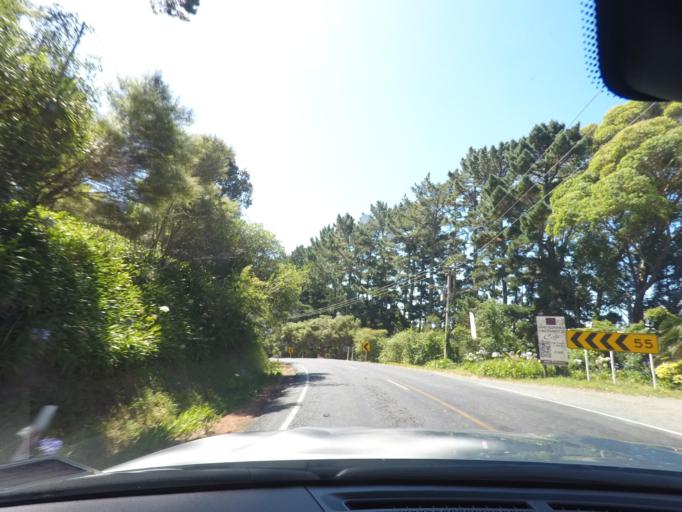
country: NZ
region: Auckland
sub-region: Auckland
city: Parakai
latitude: -36.6118
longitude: 174.3392
